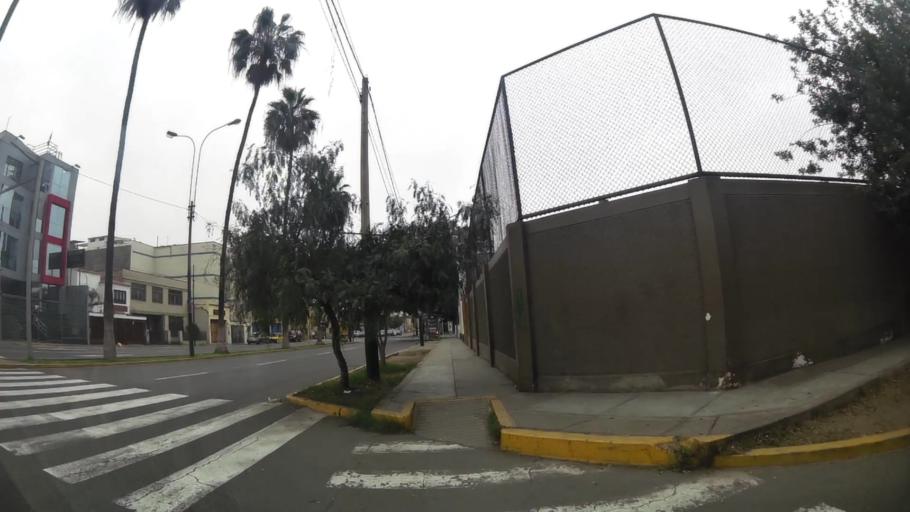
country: PE
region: Lima
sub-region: Lima
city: Surco
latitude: -12.1404
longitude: -77.0224
